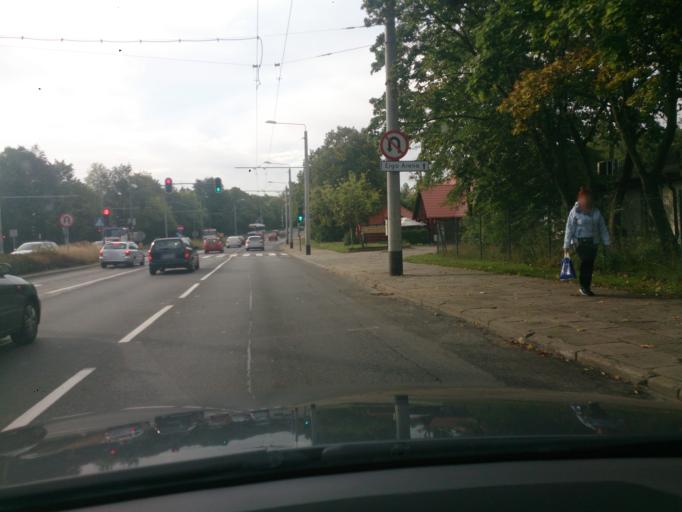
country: PL
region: Pomeranian Voivodeship
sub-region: Sopot
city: Sopot
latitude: 54.4576
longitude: 18.5553
